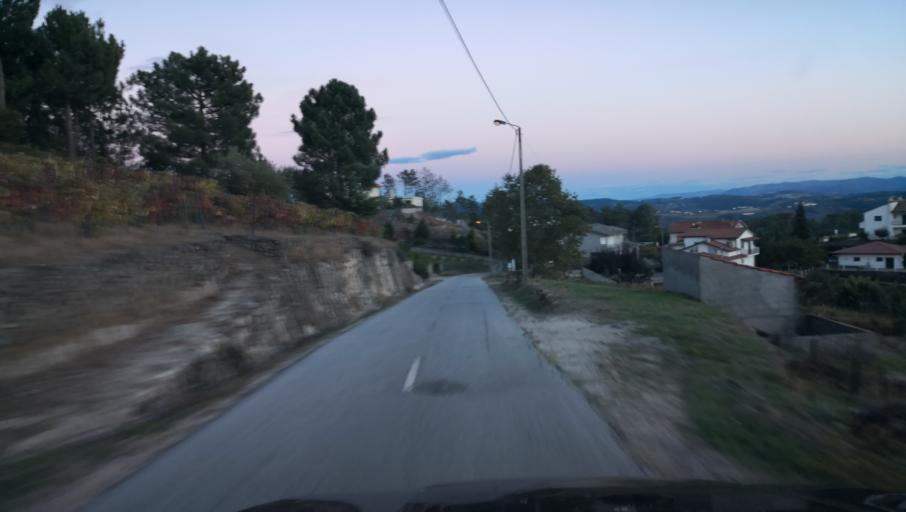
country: PT
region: Vila Real
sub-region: Santa Marta de Penaguiao
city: Santa Marta de Penaguiao
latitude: 41.2612
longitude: -7.7849
